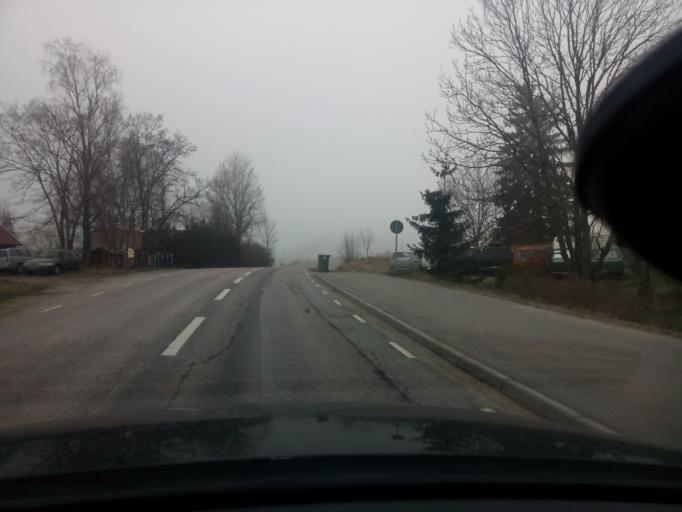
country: SE
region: Soedermanland
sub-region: Nykopings Kommun
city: Nykoping
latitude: 58.8664
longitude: 17.0667
